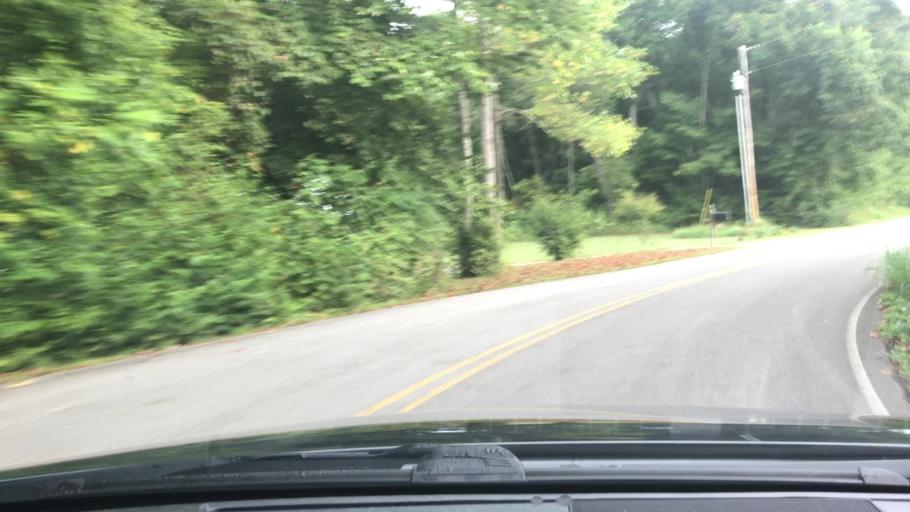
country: US
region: Tennessee
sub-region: Dickson County
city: Charlotte
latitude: 36.1919
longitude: -87.2857
